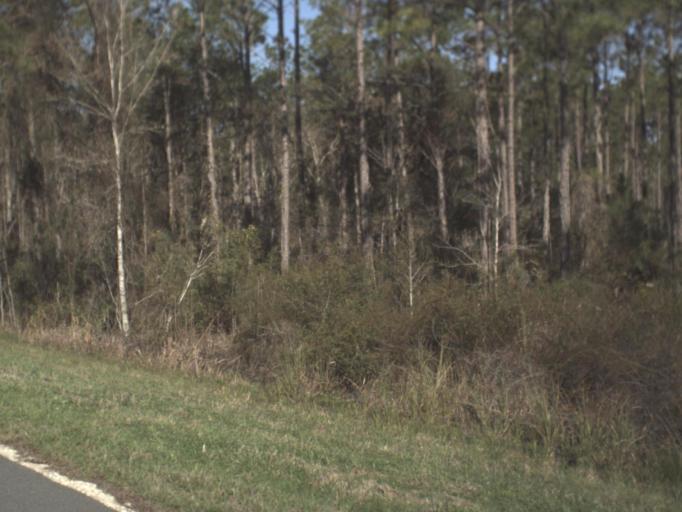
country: US
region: Florida
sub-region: Leon County
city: Woodville
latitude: 30.1889
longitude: -84.0414
